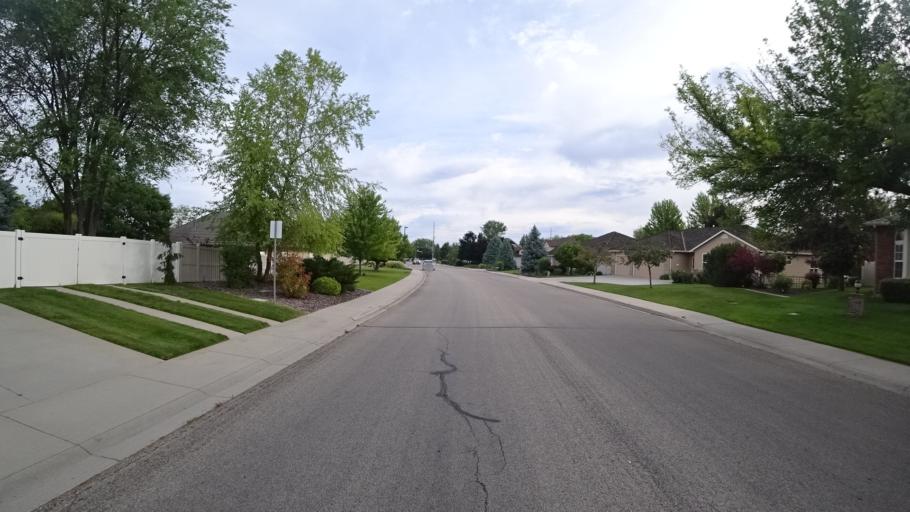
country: US
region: Idaho
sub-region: Ada County
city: Meridian
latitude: 43.5883
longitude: -116.3855
